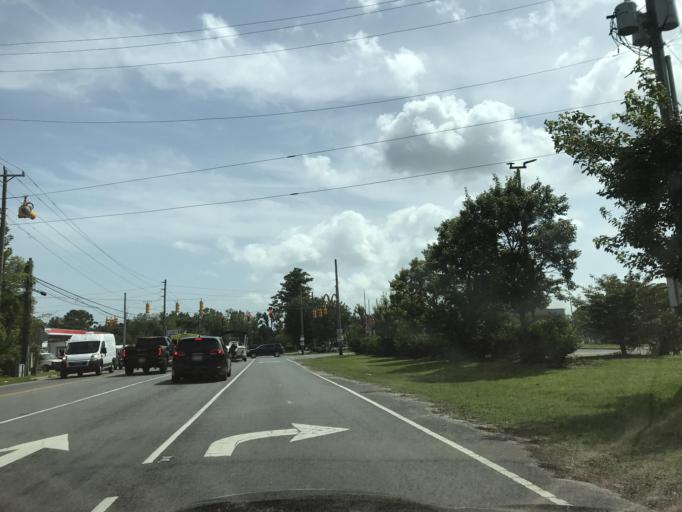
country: US
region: North Carolina
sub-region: New Hanover County
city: Wrightsboro
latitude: 34.2892
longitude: -77.9211
